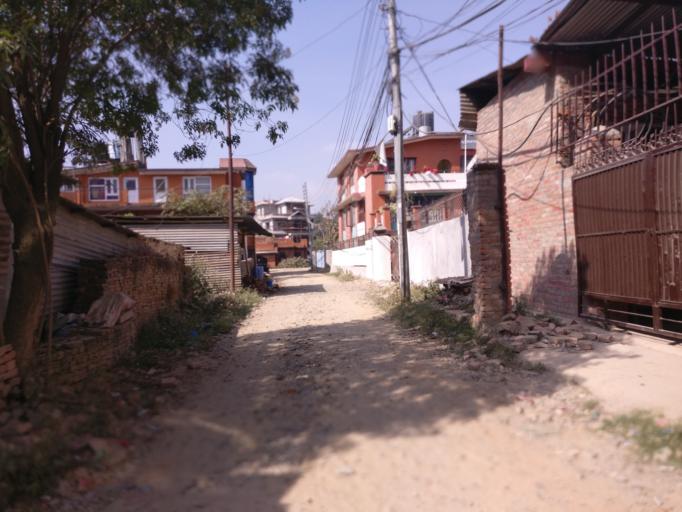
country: NP
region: Central Region
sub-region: Bagmati Zone
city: Patan
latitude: 27.6645
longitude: 85.3188
